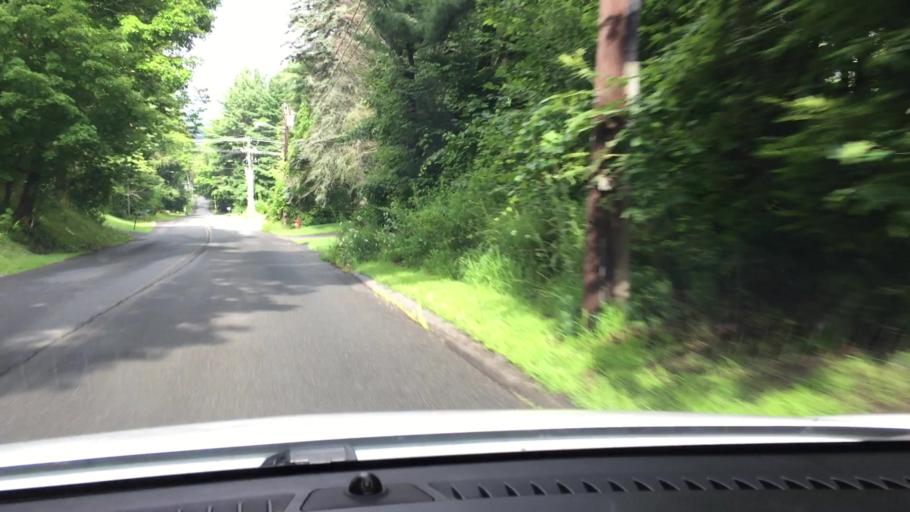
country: US
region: Massachusetts
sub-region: Berkshire County
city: Dalton
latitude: 42.4607
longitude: -73.1717
